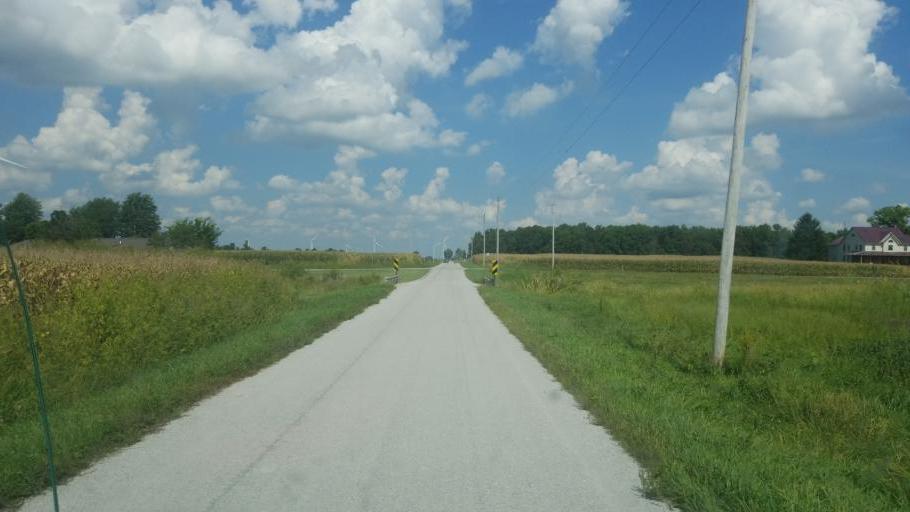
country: US
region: Ohio
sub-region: Hardin County
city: Ada
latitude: 40.7606
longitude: -83.7096
